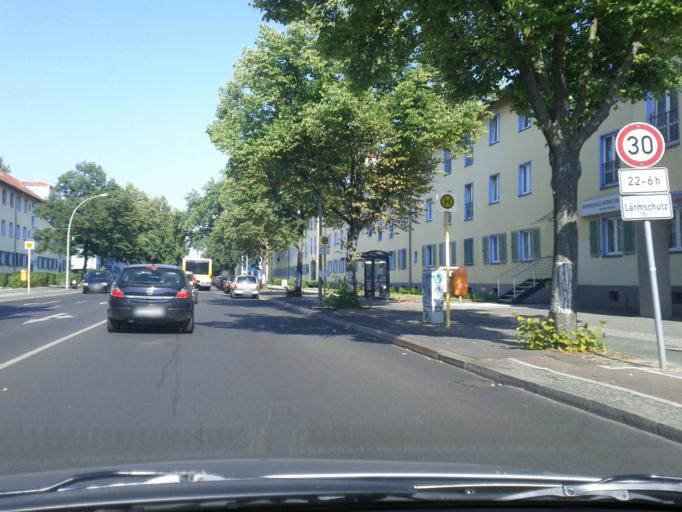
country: DE
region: Berlin
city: Kopenick Bezirk
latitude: 52.4633
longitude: 13.5835
